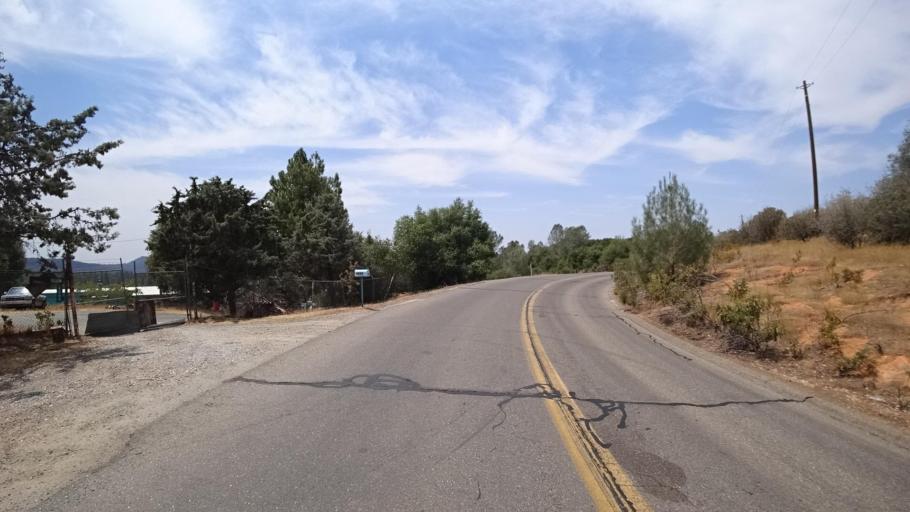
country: US
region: California
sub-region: Madera County
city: Ahwahnee
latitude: 37.4517
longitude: -119.8225
